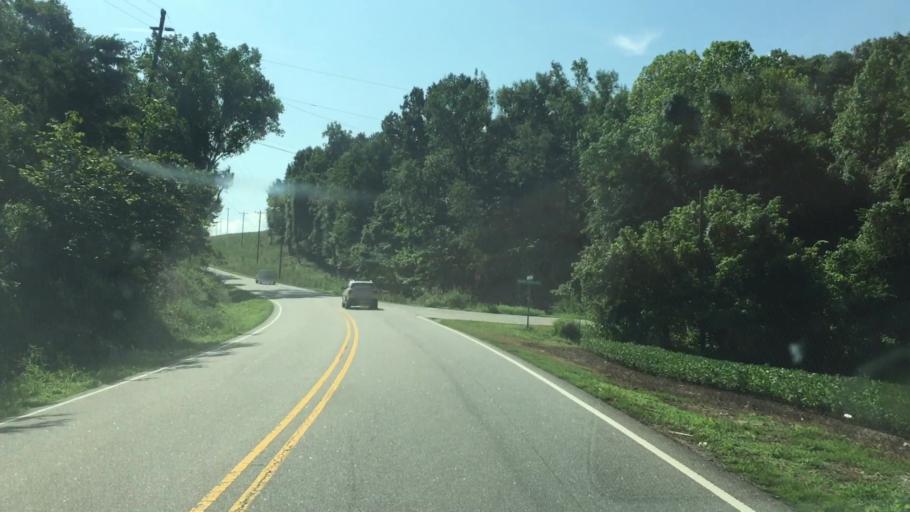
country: US
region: North Carolina
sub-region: Anson County
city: Burnsville
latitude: 35.1091
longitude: -80.3360
